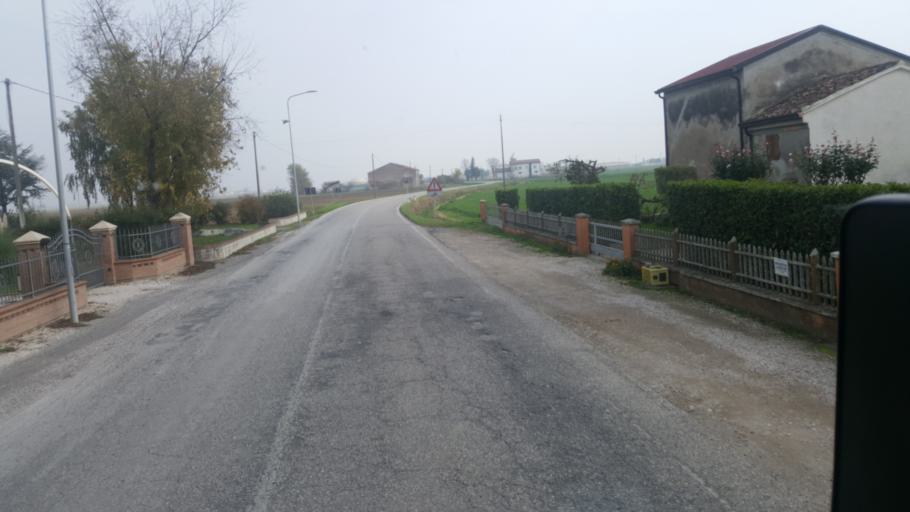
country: IT
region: Lombardy
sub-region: Provincia di Mantova
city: Magnacavallo
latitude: 44.9712
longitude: 11.1997
